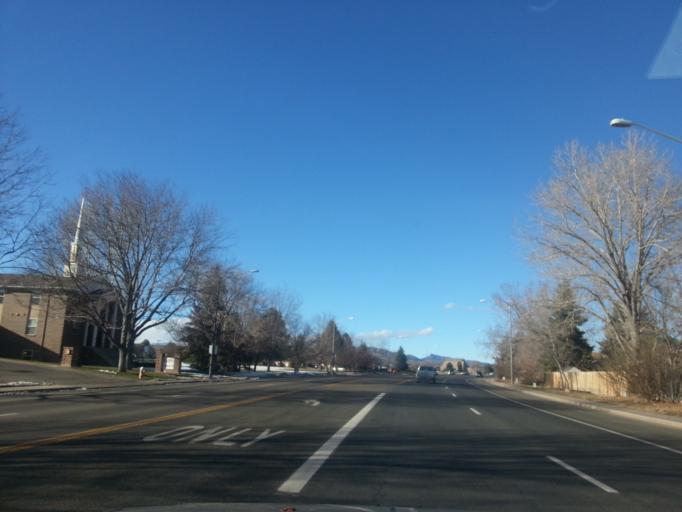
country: US
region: Colorado
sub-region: Larimer County
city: Loveland
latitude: 40.4181
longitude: -105.1142
